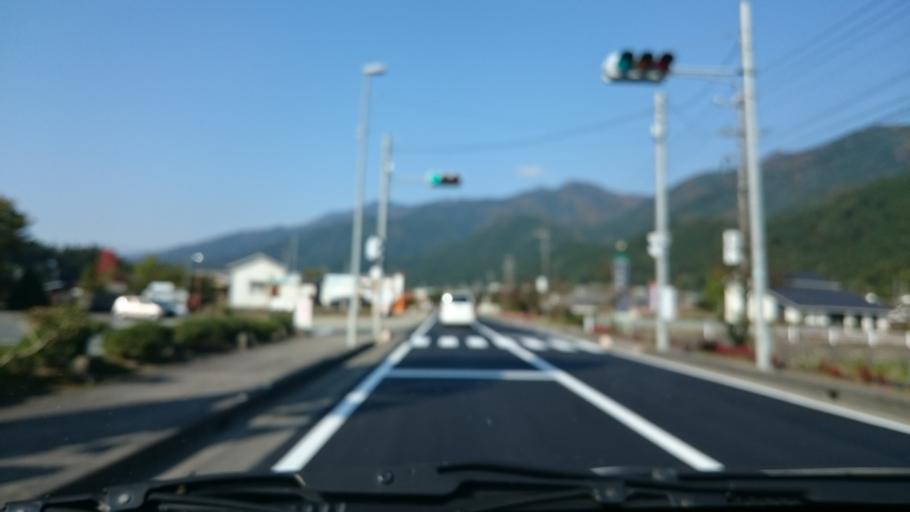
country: JP
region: Gifu
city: Nakatsugawa
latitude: 35.6962
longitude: 137.3808
